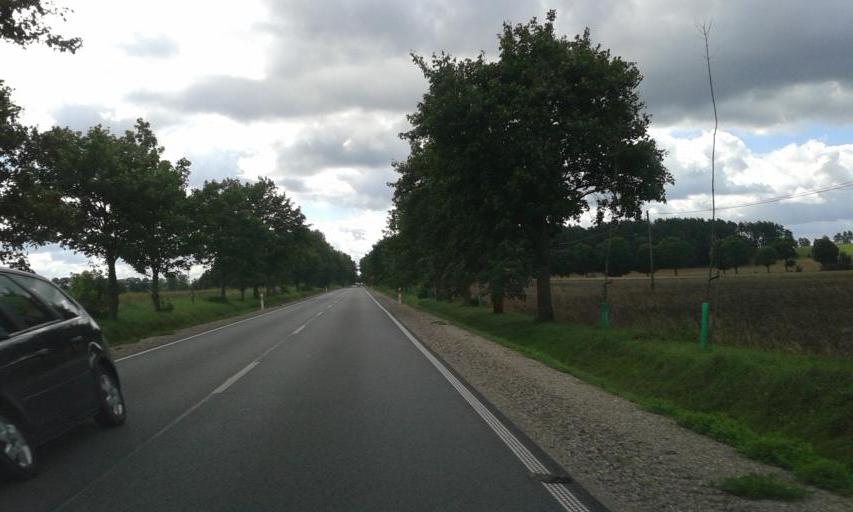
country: PL
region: West Pomeranian Voivodeship
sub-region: Powiat drawski
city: Czaplinek
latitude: 53.5096
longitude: 16.3217
